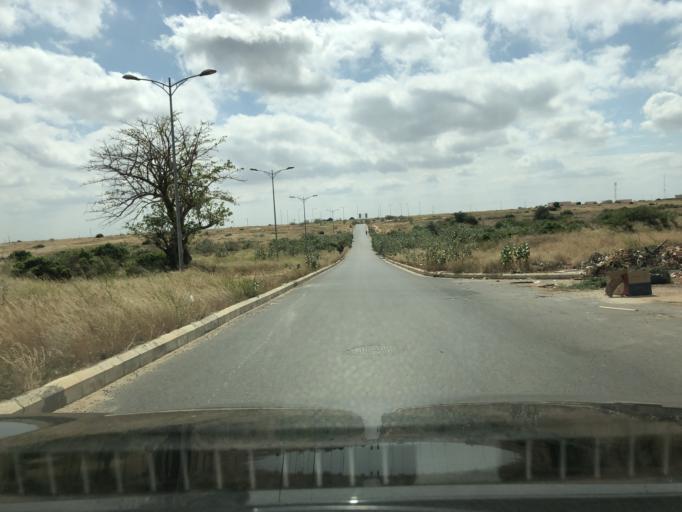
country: AO
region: Luanda
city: Luanda
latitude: -8.9664
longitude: 13.2426
